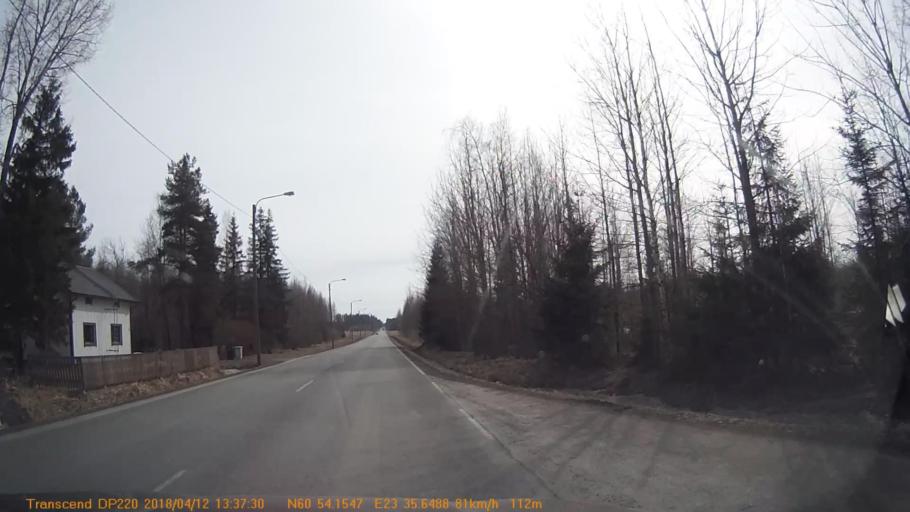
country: FI
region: Haeme
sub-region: Forssa
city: Forssa
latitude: 60.9024
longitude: 23.5942
